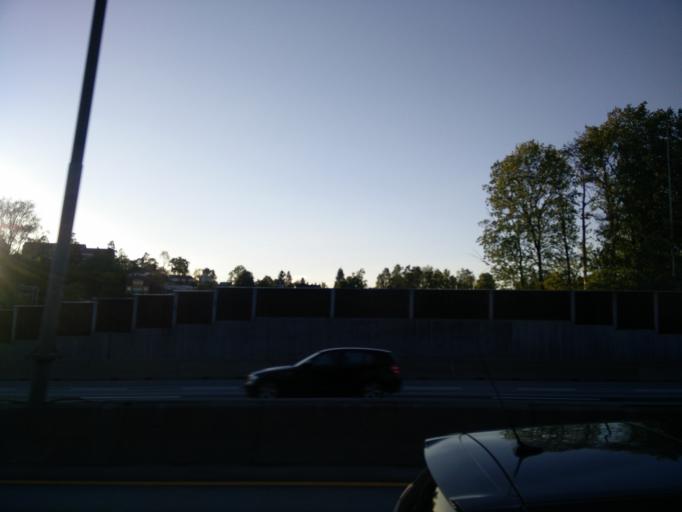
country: NO
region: Akershus
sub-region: Baerum
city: Lysaker
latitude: 59.9007
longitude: 10.5865
